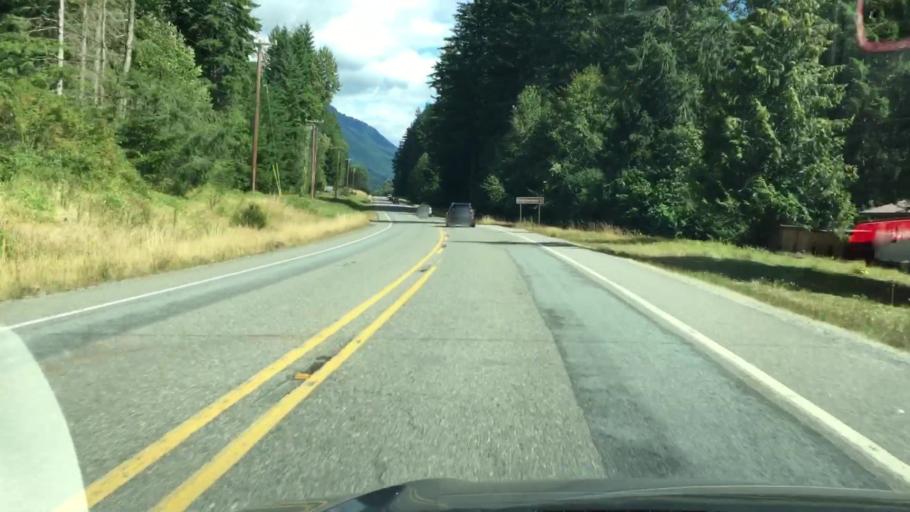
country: US
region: Washington
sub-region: Pierce County
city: Eatonville
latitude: 46.7569
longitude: -122.0234
